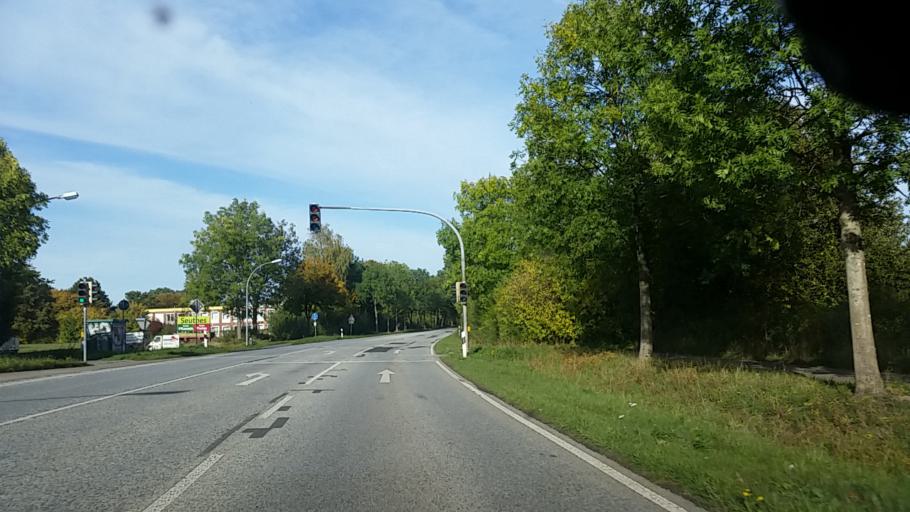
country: DE
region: Schleswig-Holstein
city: Delingsdorf
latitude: 53.6954
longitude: 10.2421
